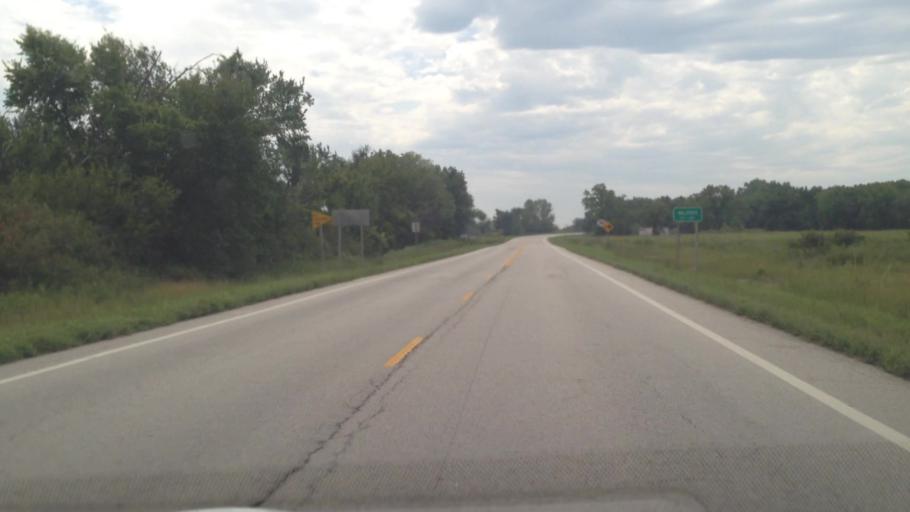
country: US
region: Kansas
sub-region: Allen County
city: Iola
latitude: 38.0260
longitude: -95.1724
